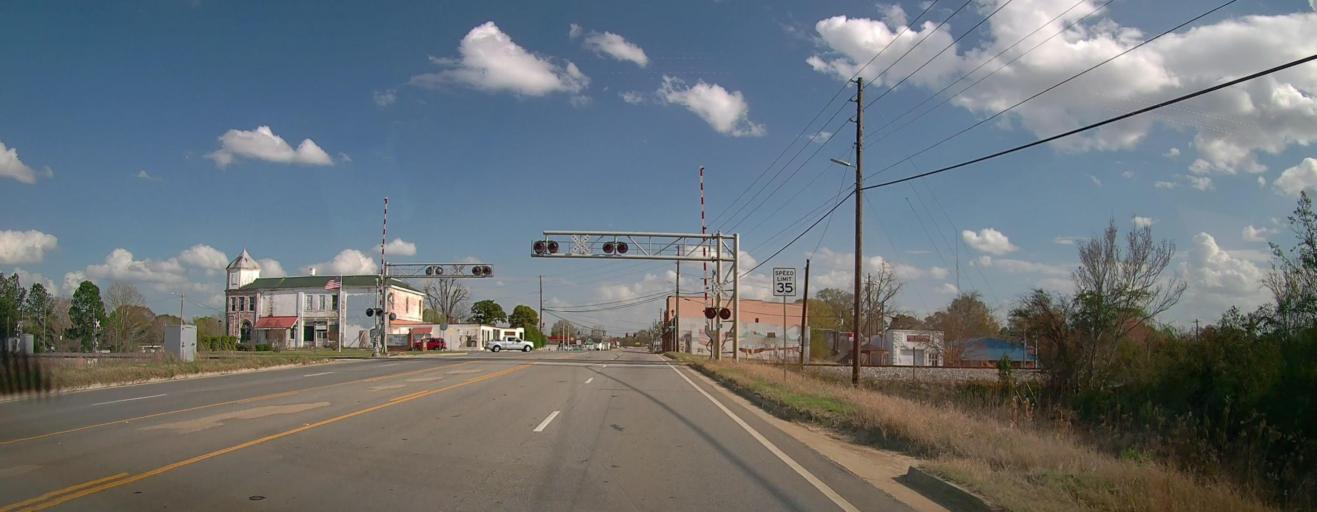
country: US
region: Georgia
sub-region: Telfair County
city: Helena
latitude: 32.0745
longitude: -82.9150
